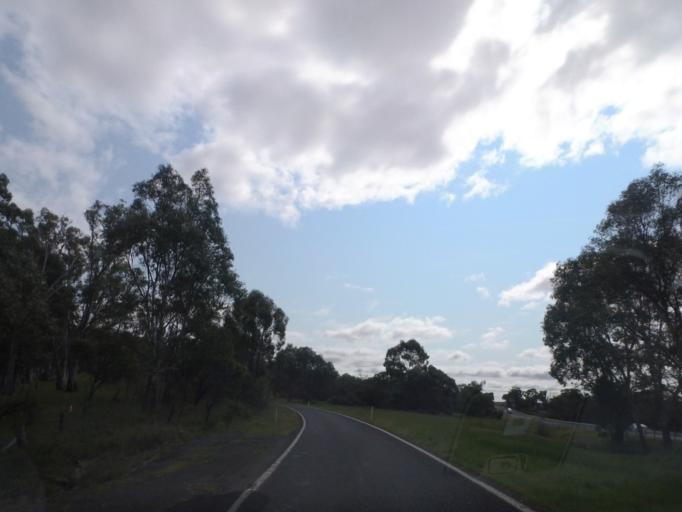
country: AU
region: Victoria
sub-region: Murrindindi
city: Kinglake West
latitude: -37.1110
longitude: 145.0915
